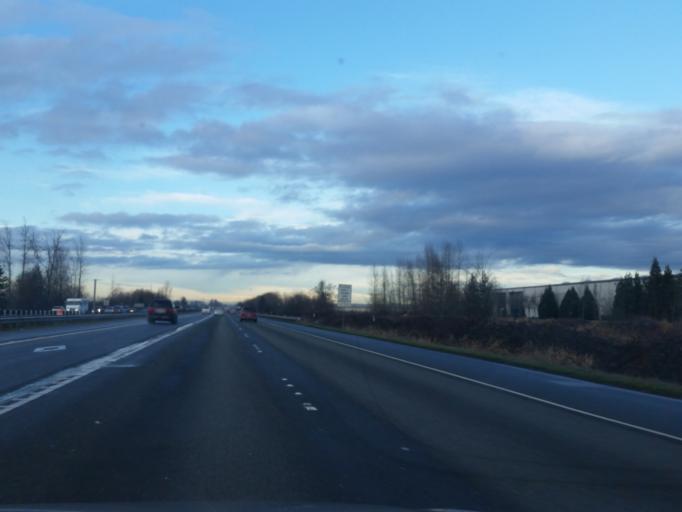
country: US
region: Washington
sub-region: King County
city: Lakeland North
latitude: 47.3411
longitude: -122.2447
